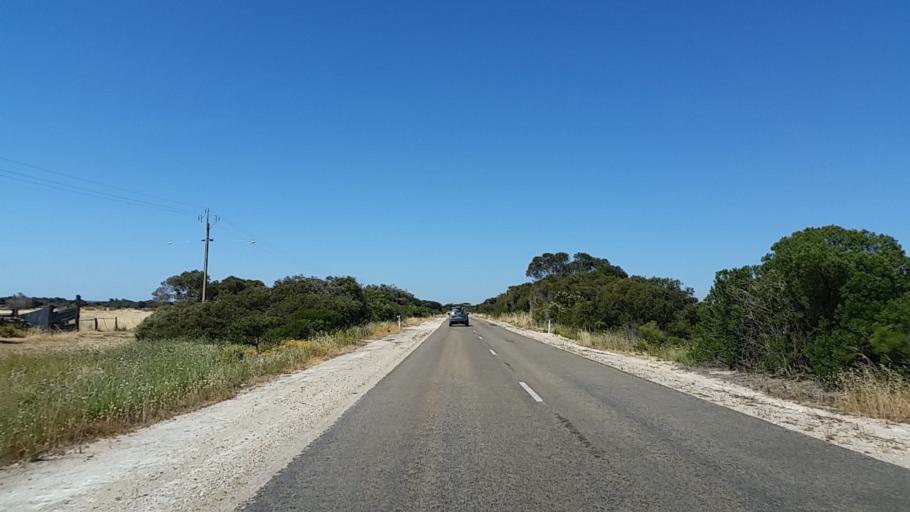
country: AU
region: South Australia
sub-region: Yorke Peninsula
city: Honiton
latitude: -35.2196
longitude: 136.9984
